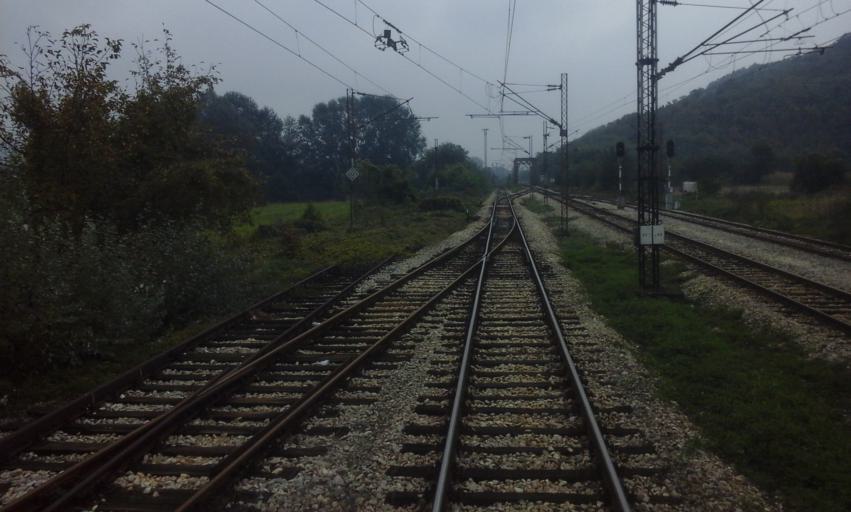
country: RS
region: Central Serbia
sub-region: Sumadijski Okrug
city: Batocina
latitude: 44.0815
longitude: 21.1832
